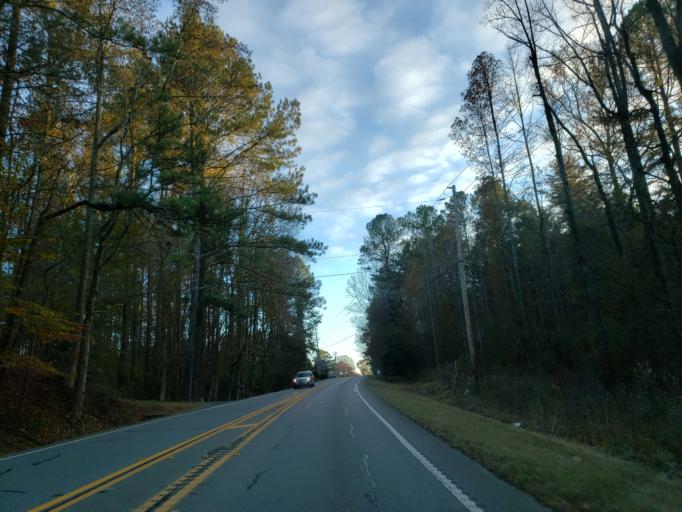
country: US
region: Georgia
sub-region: Cherokee County
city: Ball Ground
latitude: 34.2631
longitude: -84.2882
